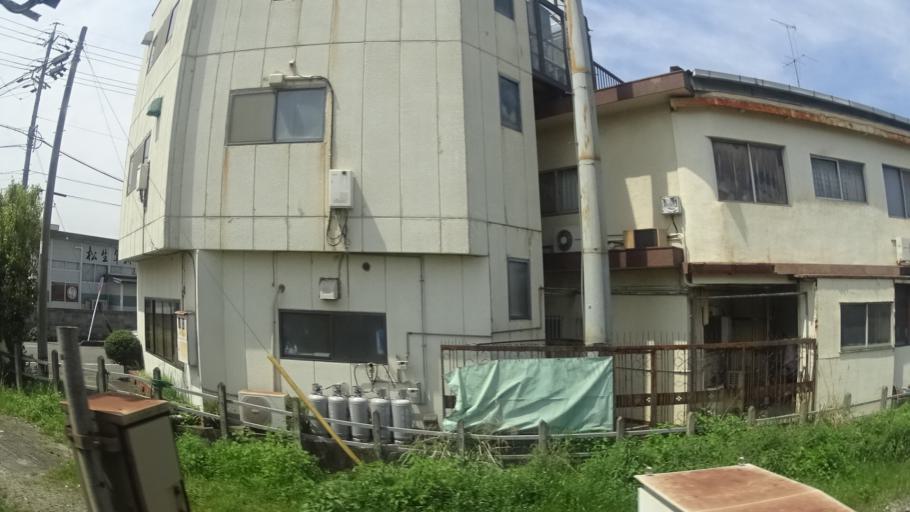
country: JP
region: Mie
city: Tsu-shi
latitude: 34.7090
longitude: 136.5006
